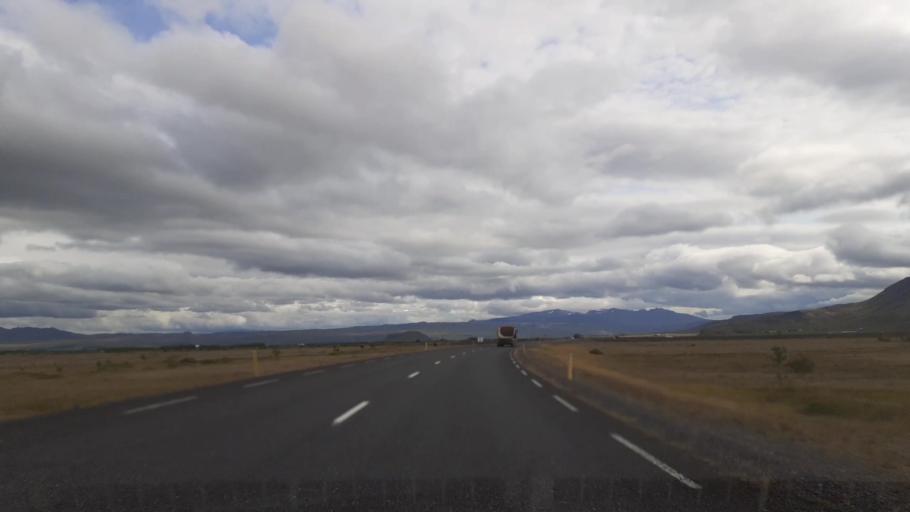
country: IS
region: South
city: Vestmannaeyjar
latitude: 63.6199
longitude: -20.0345
